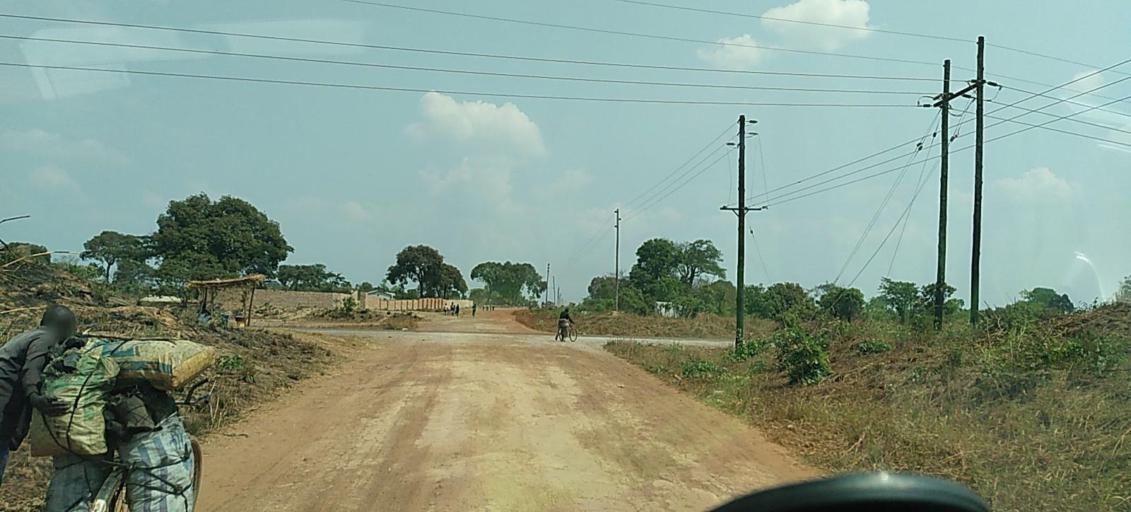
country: ZM
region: North-Western
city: Solwezi
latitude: -12.1181
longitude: 26.3680
